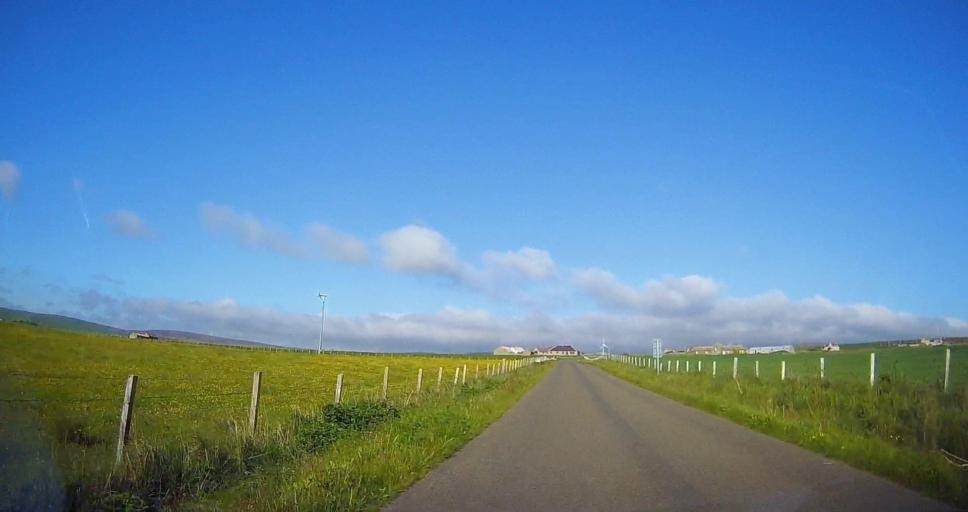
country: GB
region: Scotland
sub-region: Orkney Islands
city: Stromness
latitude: 59.0734
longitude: -3.2201
